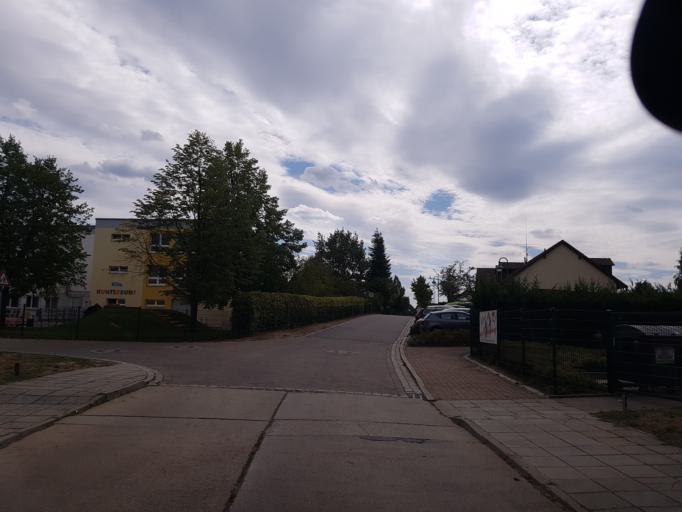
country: DE
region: Brandenburg
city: Calau
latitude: 51.7434
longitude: 13.9441
